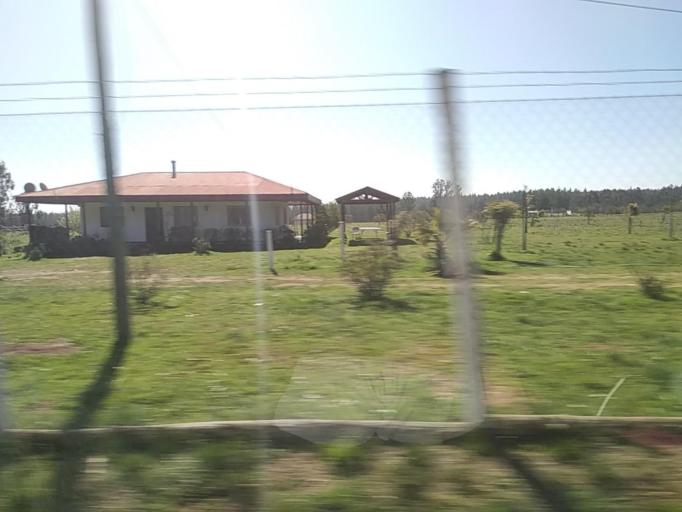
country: CL
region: Valparaiso
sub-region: San Antonio Province
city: El Tabo
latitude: -33.4097
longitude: -71.5977
